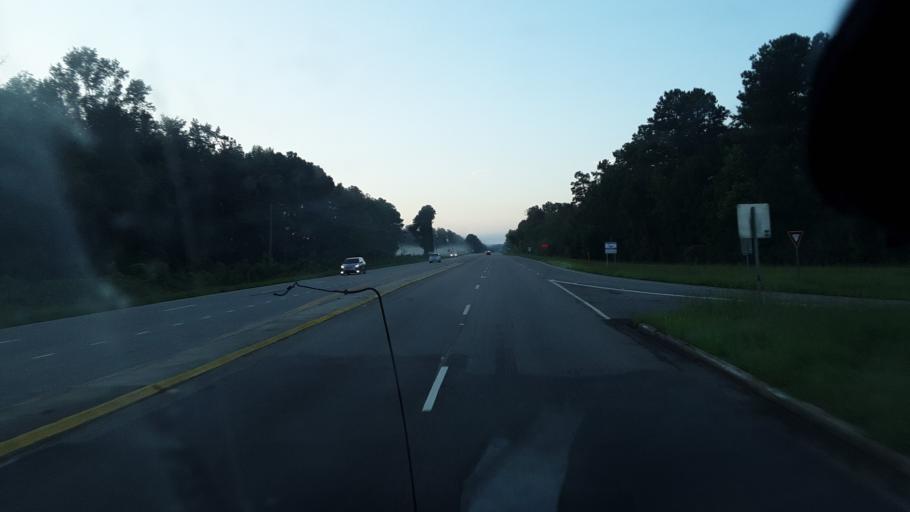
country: US
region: South Carolina
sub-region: Clarendon County
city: Manning
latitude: 33.7379
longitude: -80.2073
